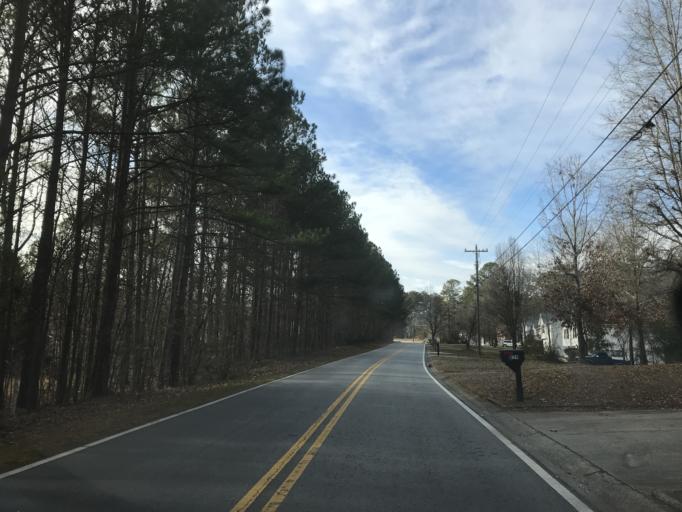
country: US
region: Georgia
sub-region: Douglas County
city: Douglasville
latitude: 33.7961
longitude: -84.8242
